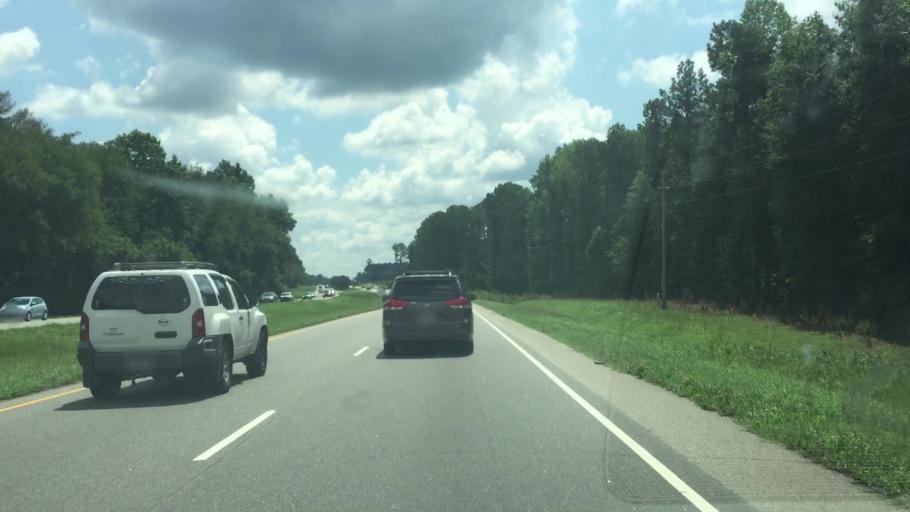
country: US
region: North Carolina
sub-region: Scotland County
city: Laurel Hill
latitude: 34.8140
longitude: -79.5655
